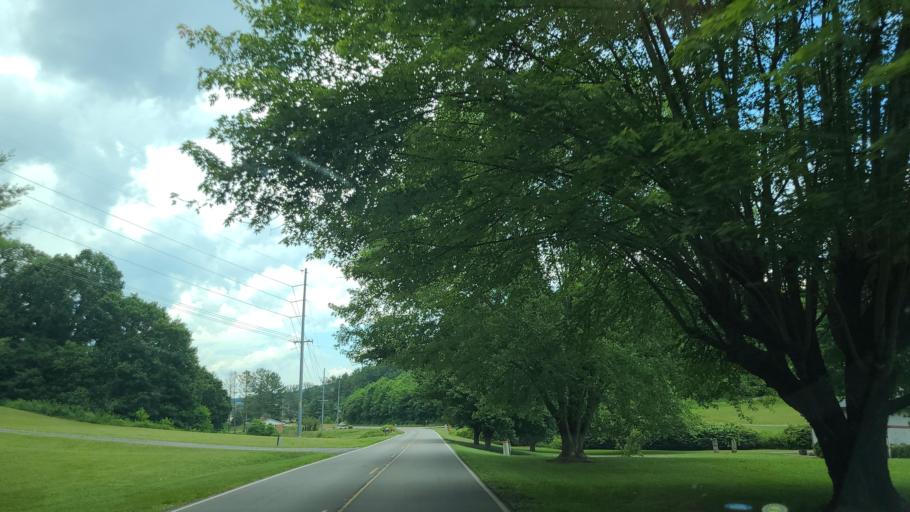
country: US
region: North Carolina
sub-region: Ashe County
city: Jefferson
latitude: 36.3935
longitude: -81.3237
